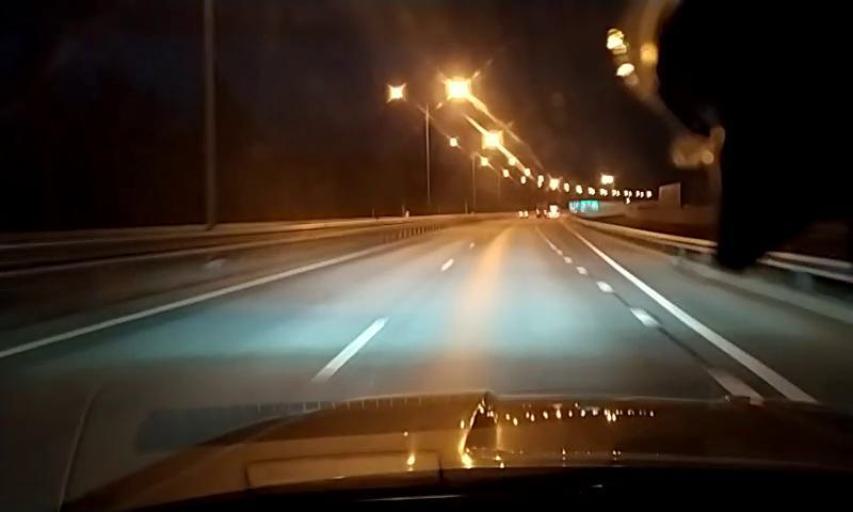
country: RU
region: Leningrad
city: Agalatovo
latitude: 60.2397
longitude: 30.3535
